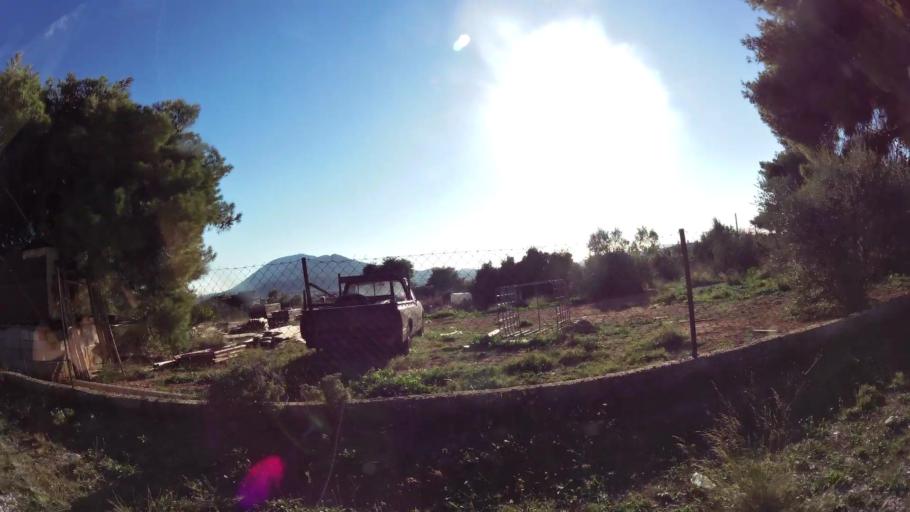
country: GR
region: Attica
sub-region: Nomarchia Anatolikis Attikis
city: Gerakas
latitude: 38.0377
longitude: 23.8573
